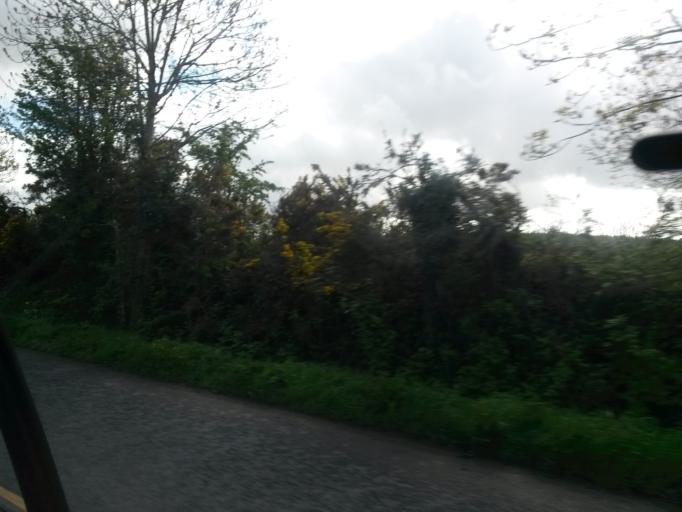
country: IE
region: Leinster
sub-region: Loch Garman
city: Ferns
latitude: 52.5678
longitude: -6.5241
